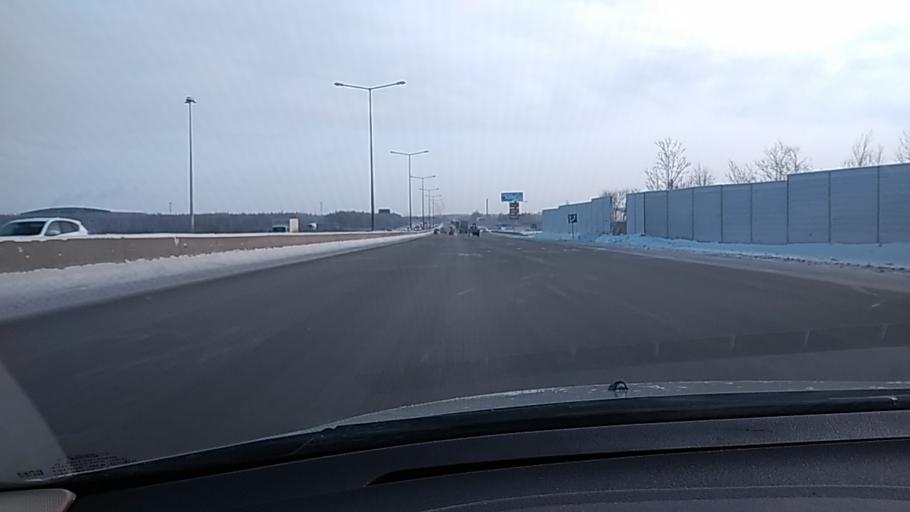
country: RU
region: Sverdlovsk
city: Istok
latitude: 56.7680
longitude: 60.7369
